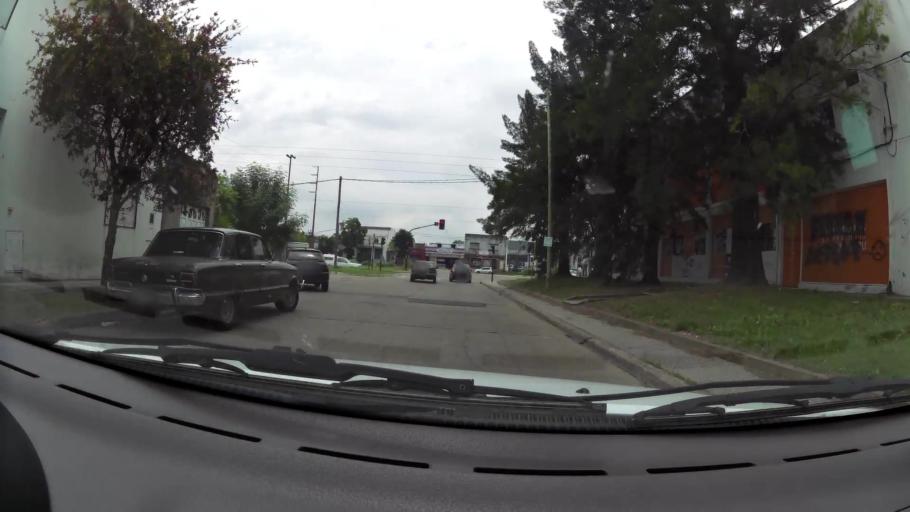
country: AR
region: Buenos Aires
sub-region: Partido de La Plata
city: La Plata
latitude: -34.9019
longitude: -57.9821
